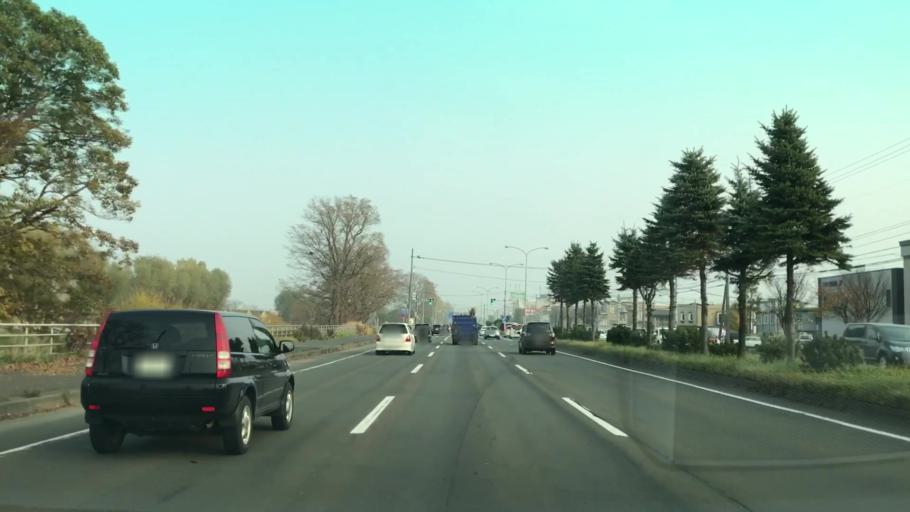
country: JP
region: Hokkaido
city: Ishikari
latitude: 43.1526
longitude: 141.3514
